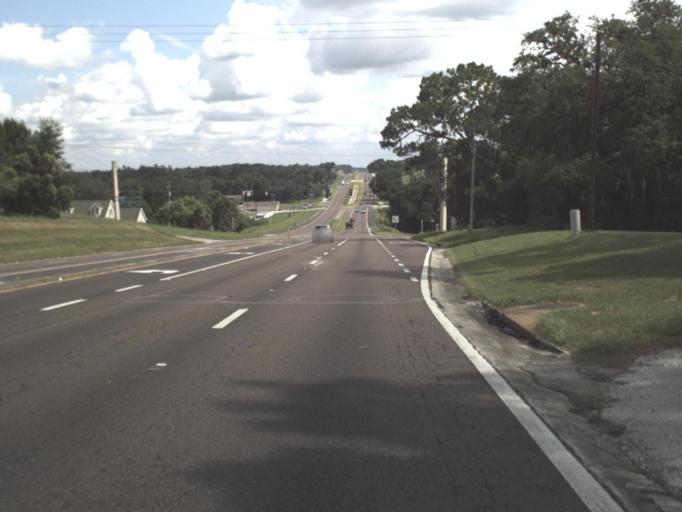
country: US
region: Florida
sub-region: Pasco County
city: Zephyrhills North
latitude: 28.3017
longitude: -82.1876
